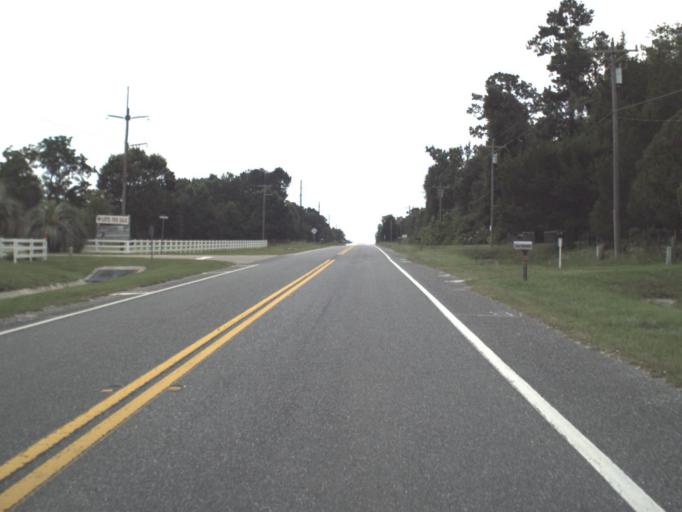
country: US
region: Florida
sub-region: Union County
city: Lake Butler
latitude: 29.9965
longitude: -82.2709
